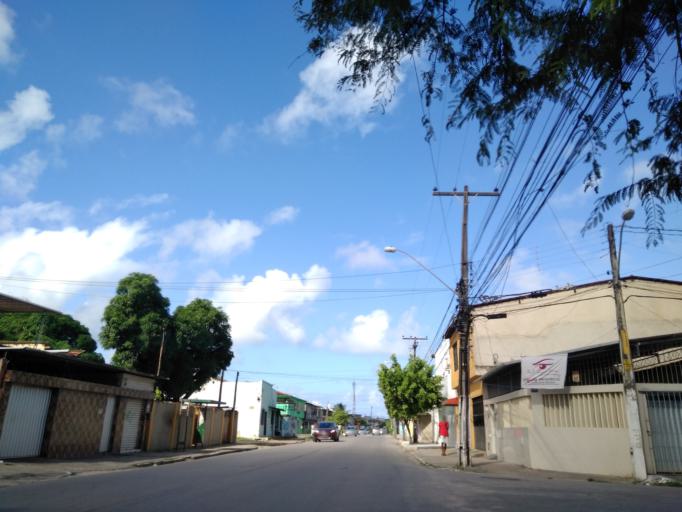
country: BR
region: Pernambuco
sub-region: Recife
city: Recife
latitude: -8.0766
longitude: -34.9128
